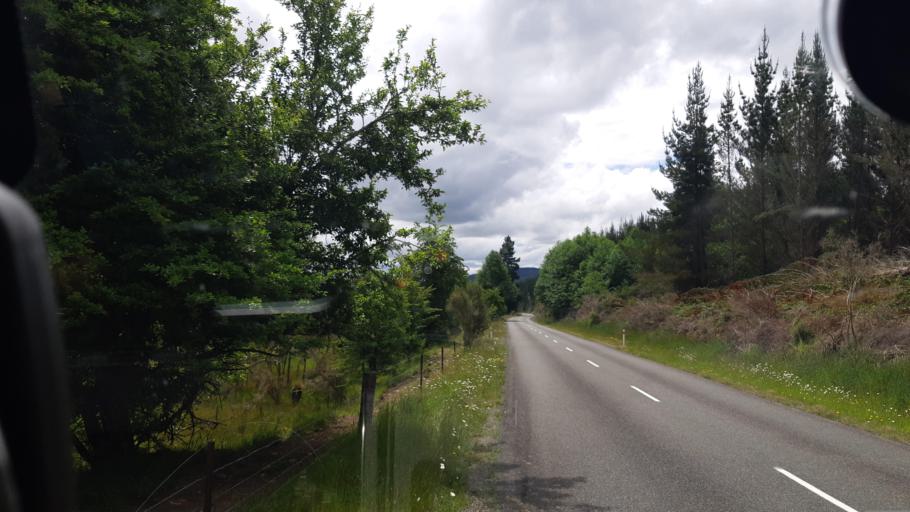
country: NZ
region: Tasman
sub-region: Tasman District
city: Wakefield
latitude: -41.6634
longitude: 172.8712
